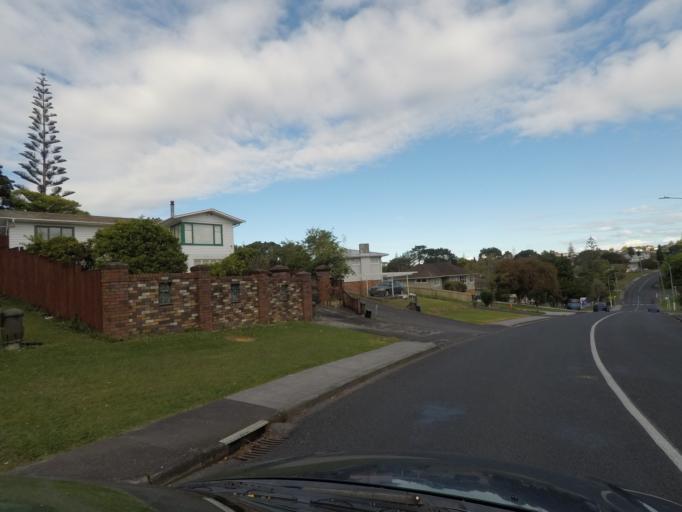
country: NZ
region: Auckland
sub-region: Auckland
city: Rosebank
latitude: -36.8863
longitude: 174.6501
